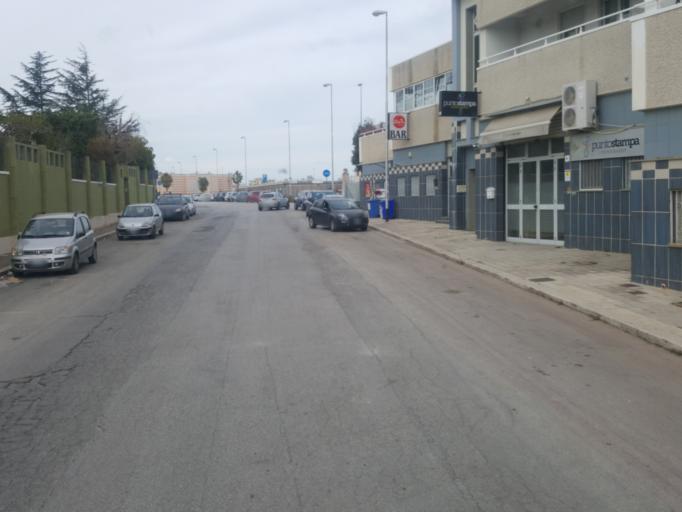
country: IT
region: Apulia
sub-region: Provincia di Barletta - Andria - Trani
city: Bisceglie
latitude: 41.2271
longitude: 16.5039
